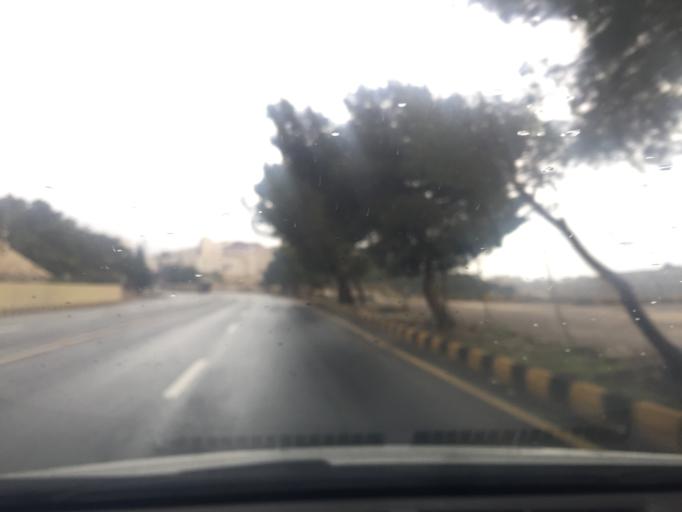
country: JO
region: Amman
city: Amman
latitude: 32.0124
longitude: 35.9339
